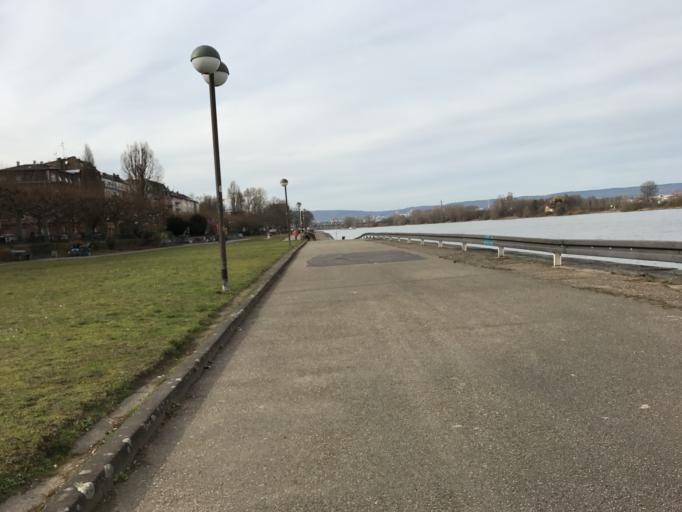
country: DE
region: Rheinland-Pfalz
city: Mainz
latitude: 50.0105
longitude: 8.2686
